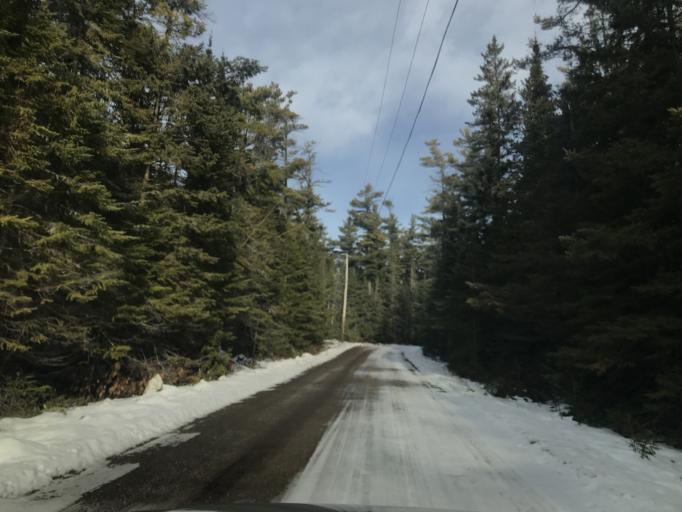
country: US
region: Wisconsin
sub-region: Door County
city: Sturgeon Bay
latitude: 45.1412
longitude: -87.0416
